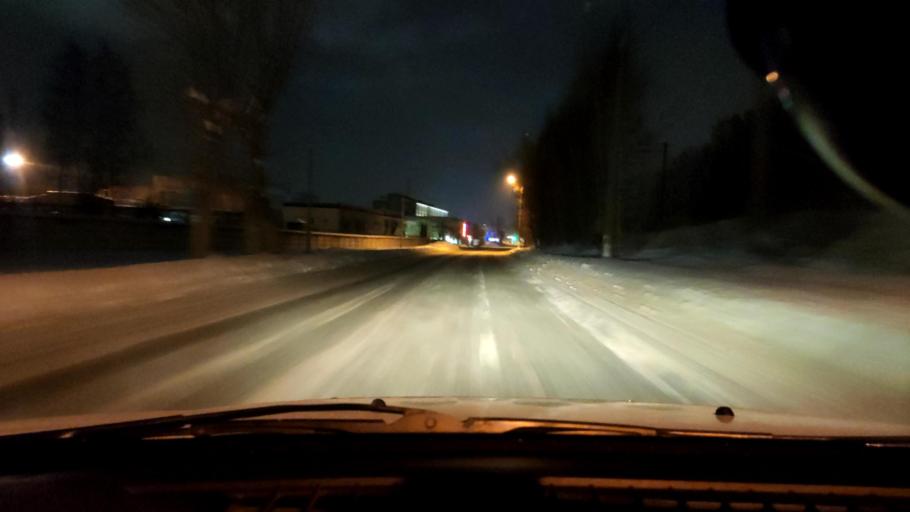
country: RU
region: Perm
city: Perm
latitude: 58.0905
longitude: 56.3535
